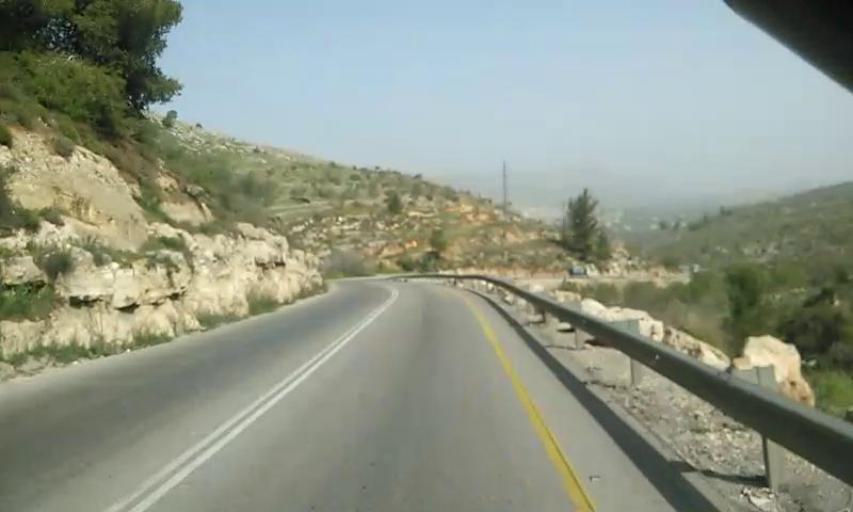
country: PS
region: West Bank
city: Yatma
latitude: 32.1237
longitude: 35.2557
